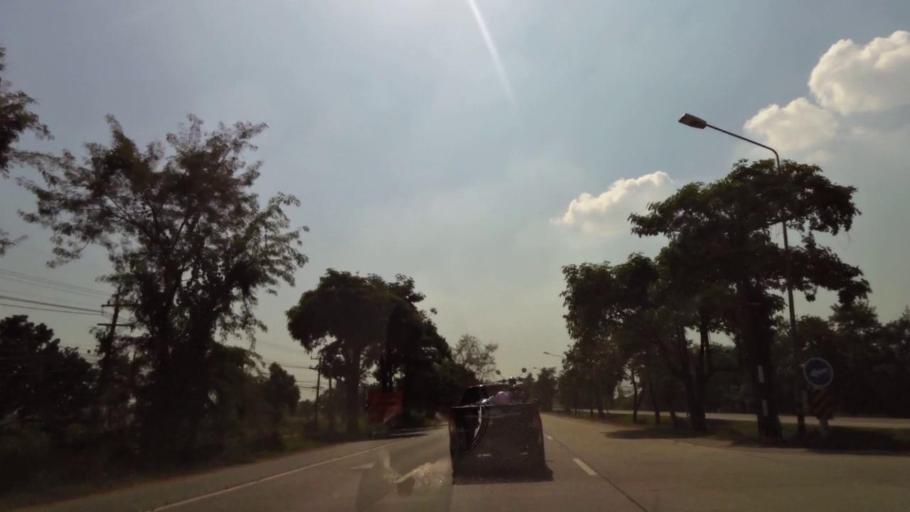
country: TH
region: Phichit
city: Wachira Barami
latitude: 16.5474
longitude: 100.1460
